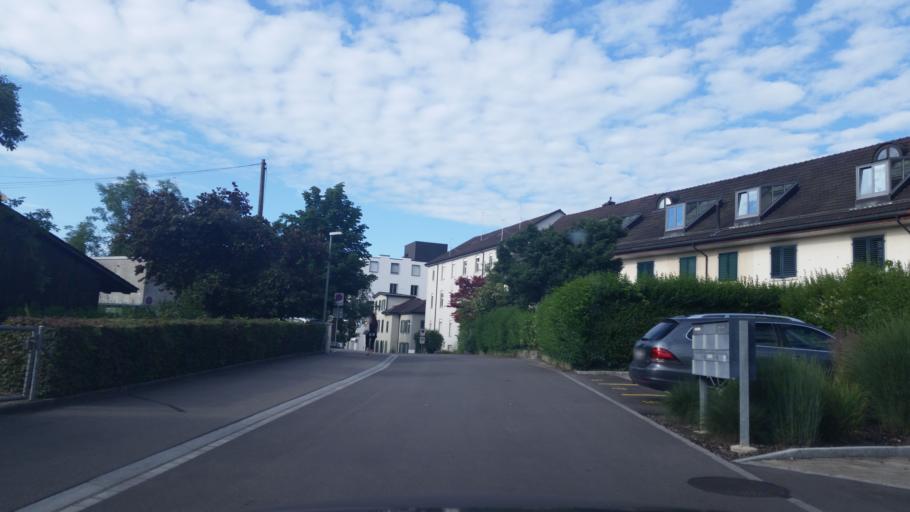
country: CH
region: Thurgau
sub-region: Frauenfeld District
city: Frauenfeld
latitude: 47.5529
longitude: 8.8966
